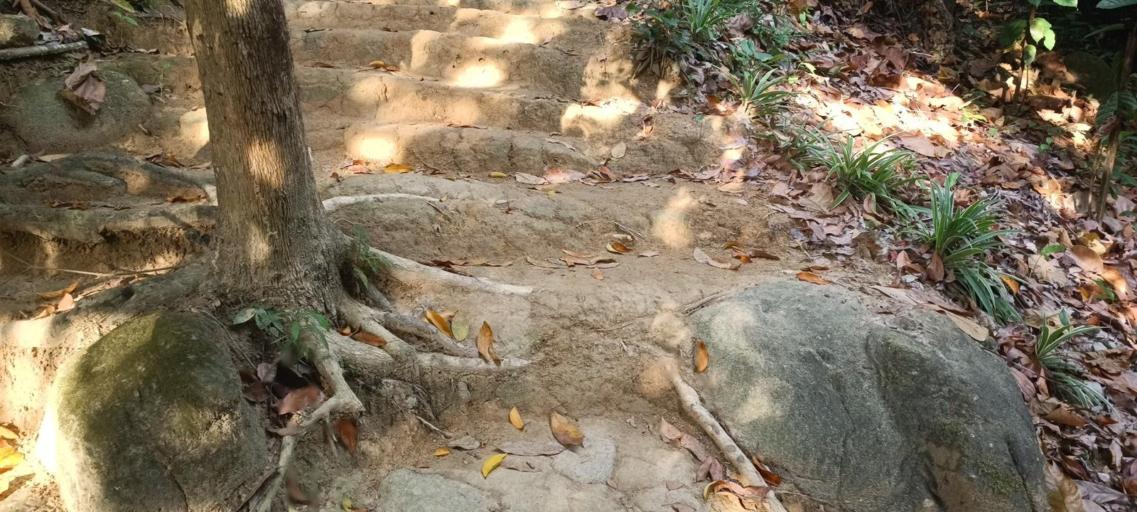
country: MY
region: Penang
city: Juru
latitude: 5.3362
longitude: 100.4145
